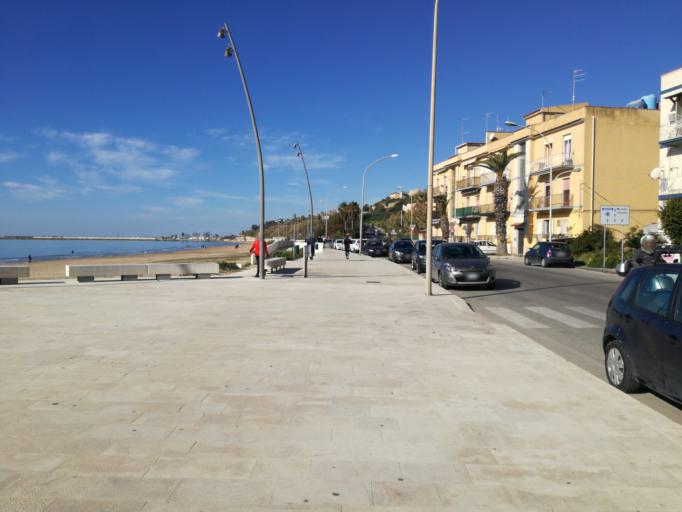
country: IT
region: Sicily
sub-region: Provincia di Caltanissetta
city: Gela
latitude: 37.0658
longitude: 14.2436
